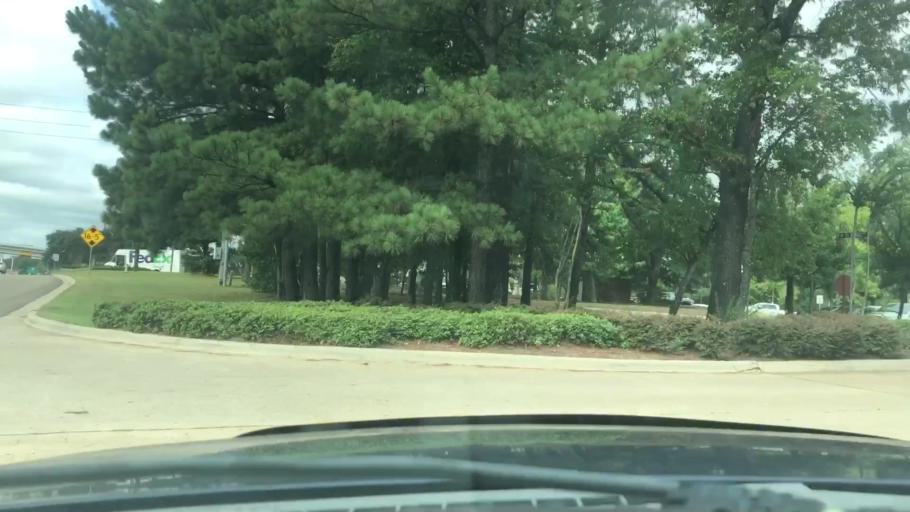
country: US
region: Arkansas
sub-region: Miller County
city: Texarkana
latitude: 33.4623
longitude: -94.0753
